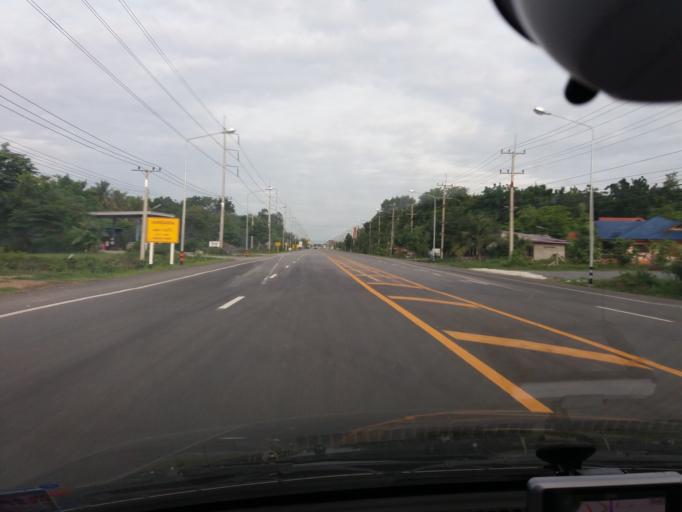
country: TH
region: Suphan Buri
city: U Thong
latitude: 14.3350
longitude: 99.7871
